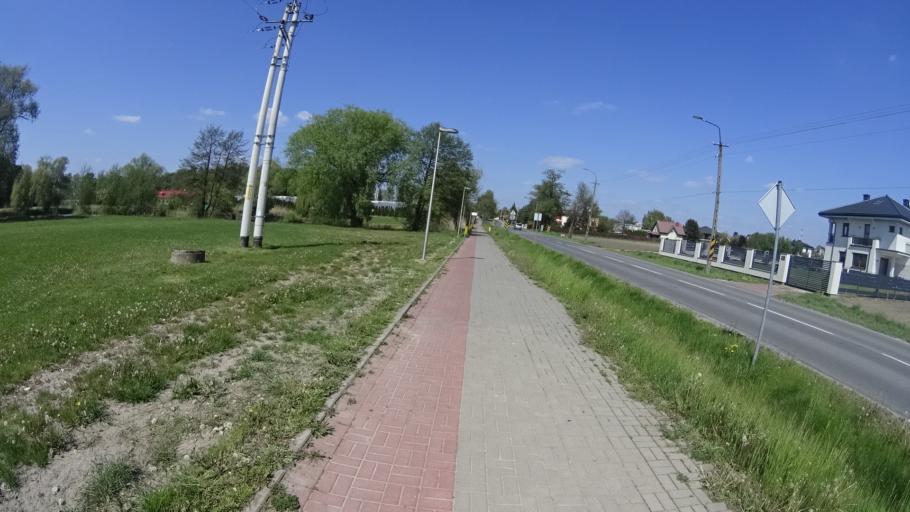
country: PL
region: Masovian Voivodeship
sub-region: Powiat warszawski zachodni
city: Stare Babice
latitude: 52.2488
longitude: 20.8203
